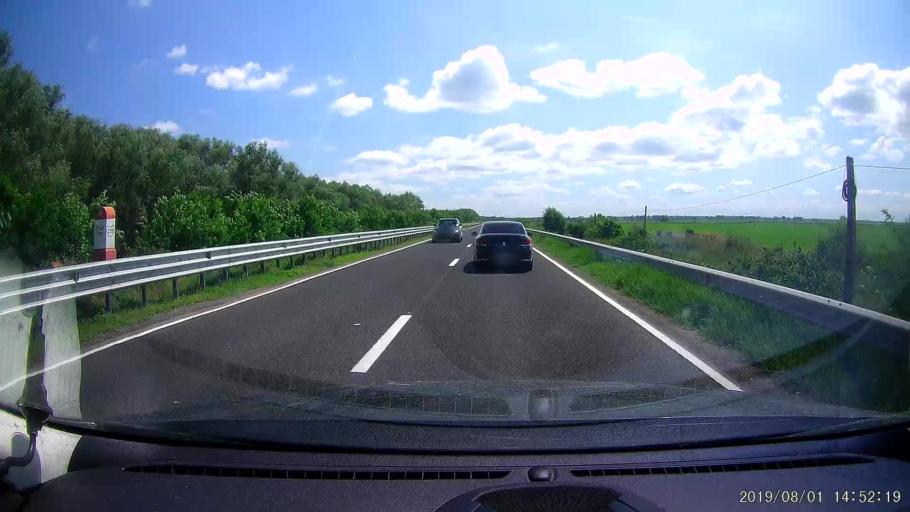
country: RO
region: Braila
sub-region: Comuna Vadeni
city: Vadeni
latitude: 45.3576
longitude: 28.0115
